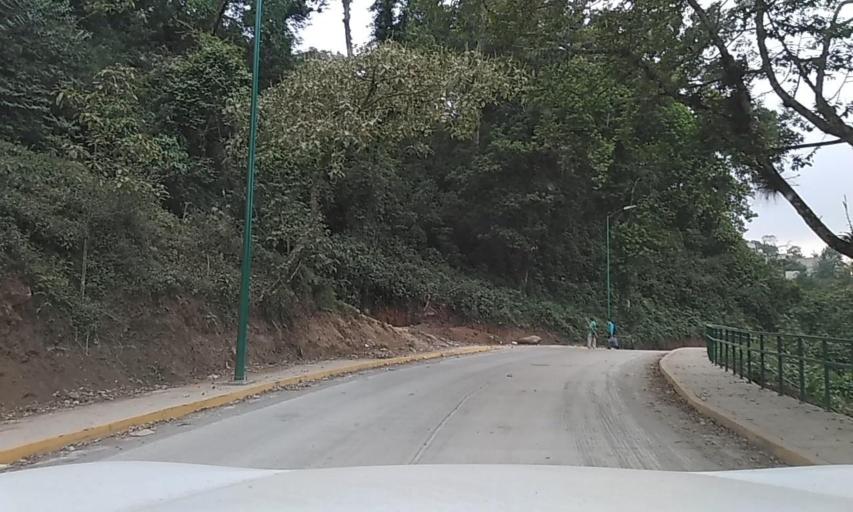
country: MX
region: Veracruz
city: El Castillo
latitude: 19.5711
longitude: -96.8904
